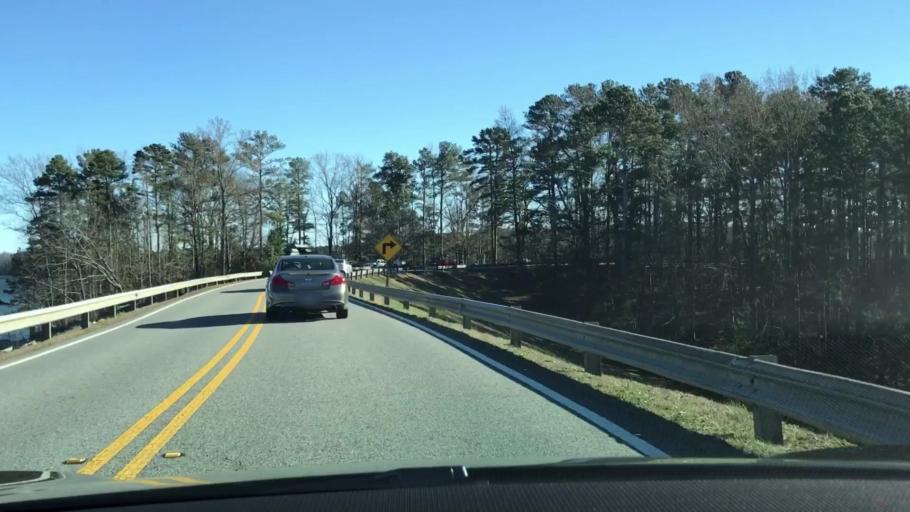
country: US
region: Georgia
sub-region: Gwinnett County
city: Sugar Hill
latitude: 34.1658
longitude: -84.0766
